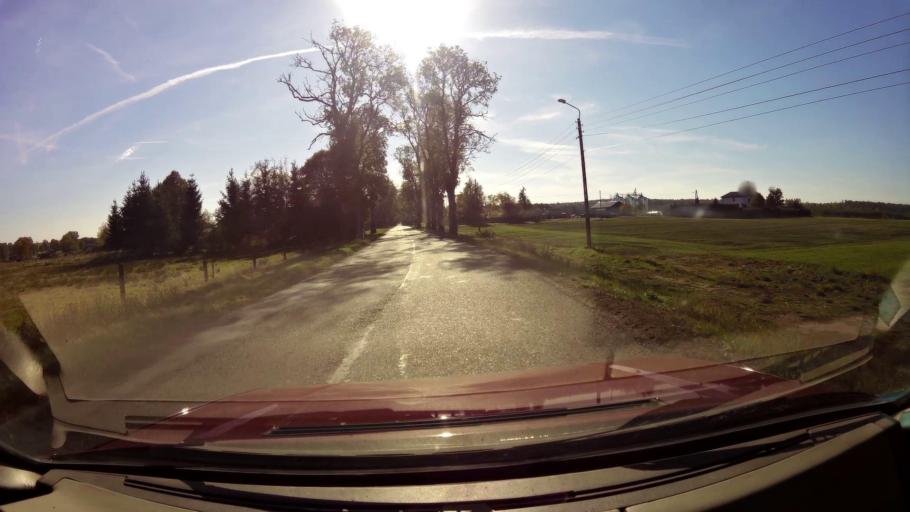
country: PL
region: West Pomeranian Voivodeship
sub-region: Powiat bialogardzki
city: Tychowo
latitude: 53.9147
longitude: 16.2391
